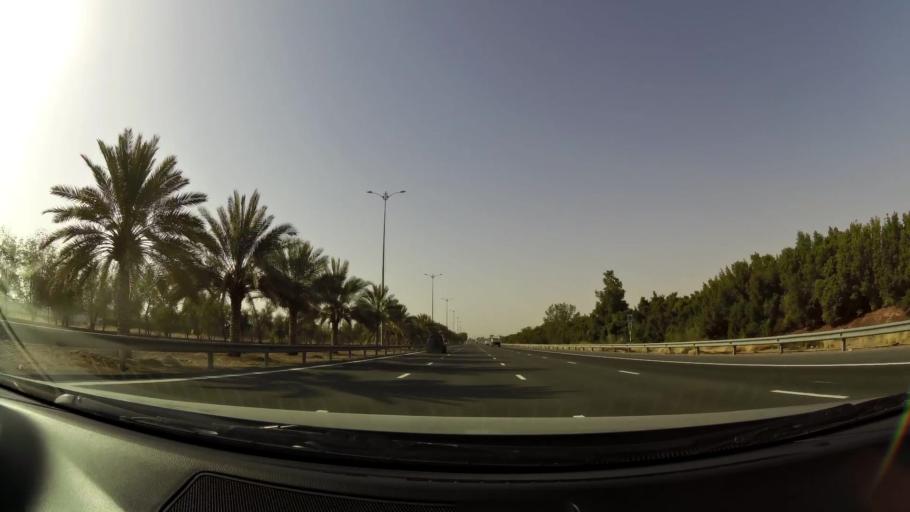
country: OM
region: Al Buraimi
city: Al Buraymi
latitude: 24.6064
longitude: 55.7308
